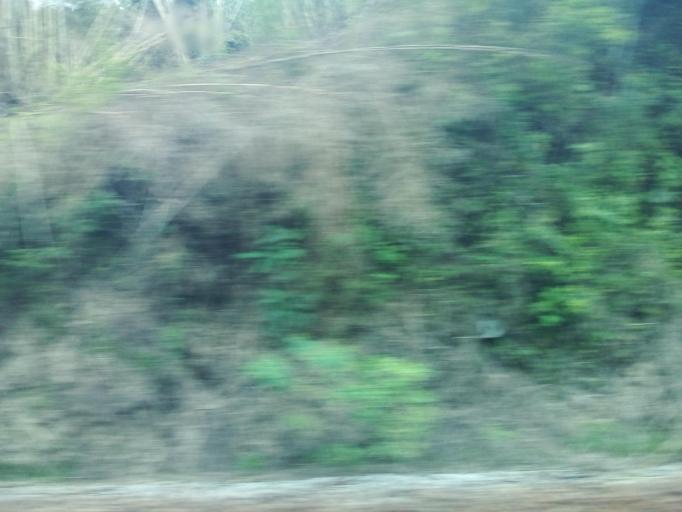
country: BR
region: Minas Gerais
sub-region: Rio Piracicaba
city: Rio Piracicaba
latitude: -19.9635
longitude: -43.2664
